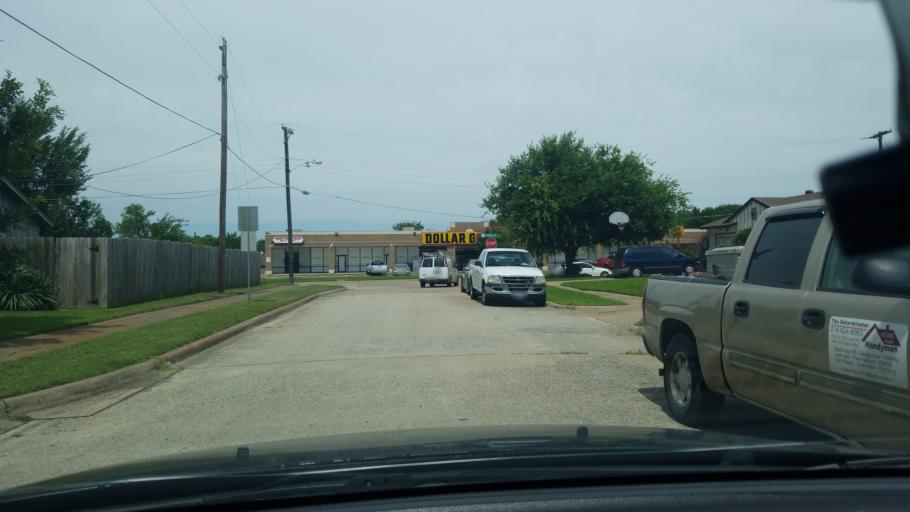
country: US
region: Texas
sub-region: Dallas County
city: Mesquite
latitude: 32.7592
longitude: -96.5829
